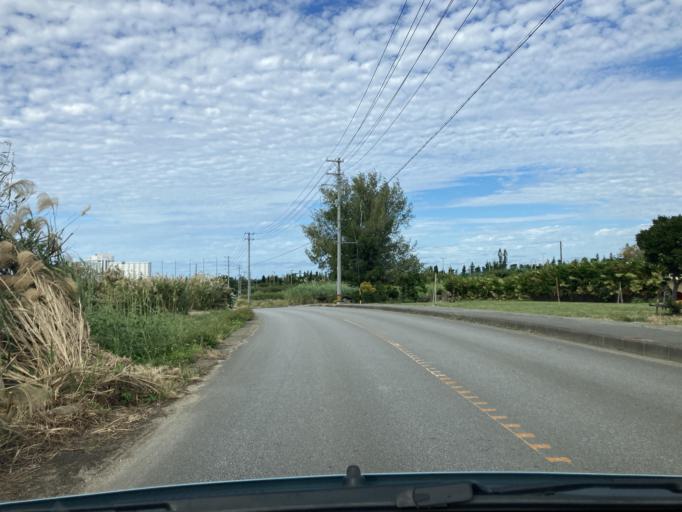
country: JP
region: Okinawa
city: Ishikawa
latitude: 26.4327
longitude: 127.7268
